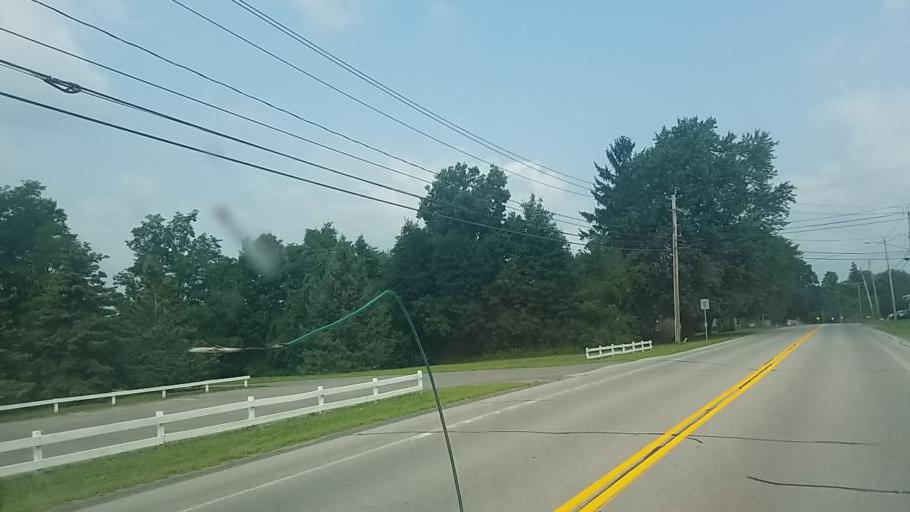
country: US
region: New York
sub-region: Montgomery County
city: Fort Plain
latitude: 42.9400
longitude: -74.6172
